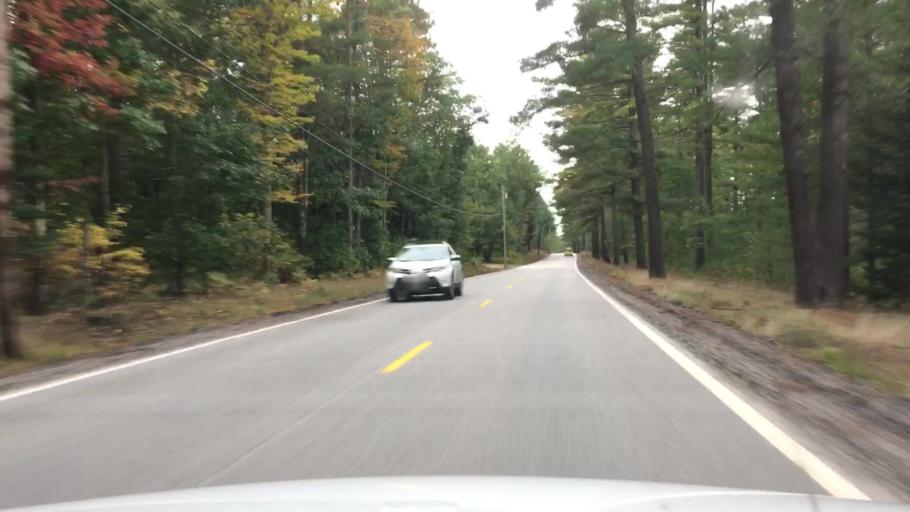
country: US
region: Maine
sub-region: Cumberland County
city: Harrison
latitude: 44.2214
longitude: -70.6931
